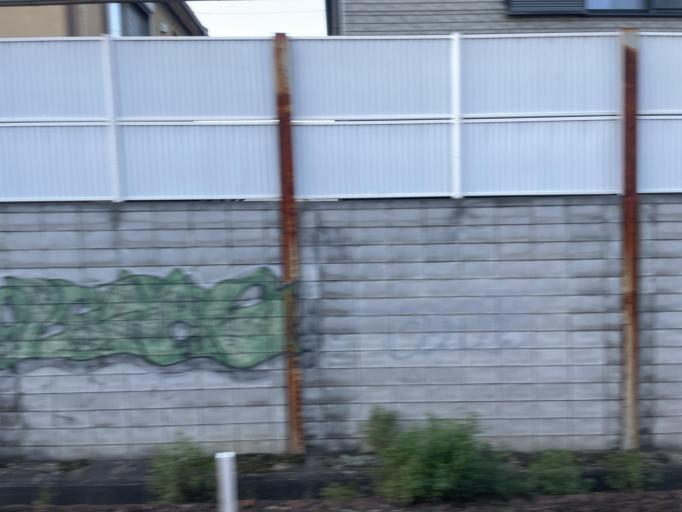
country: JP
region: Osaka
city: Matsubara
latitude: 34.5755
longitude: 135.5532
